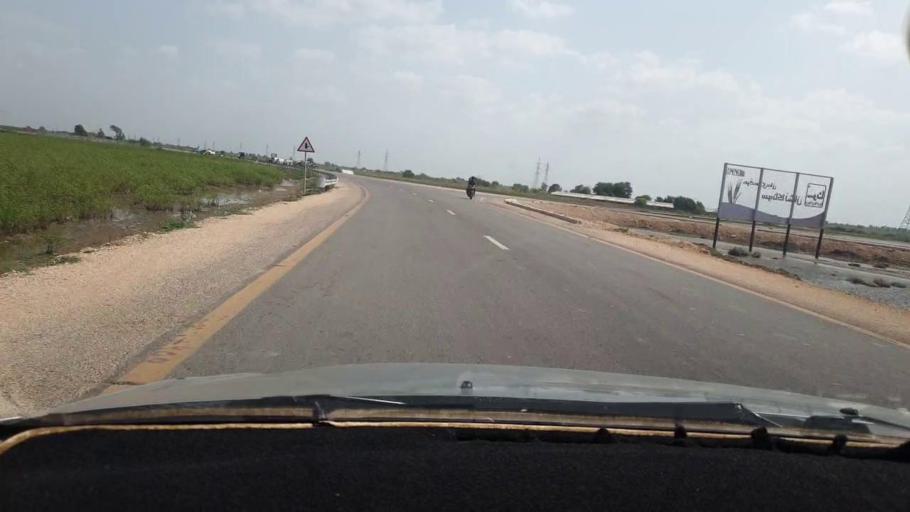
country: PK
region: Sindh
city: Digri
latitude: 25.0530
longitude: 69.2220
